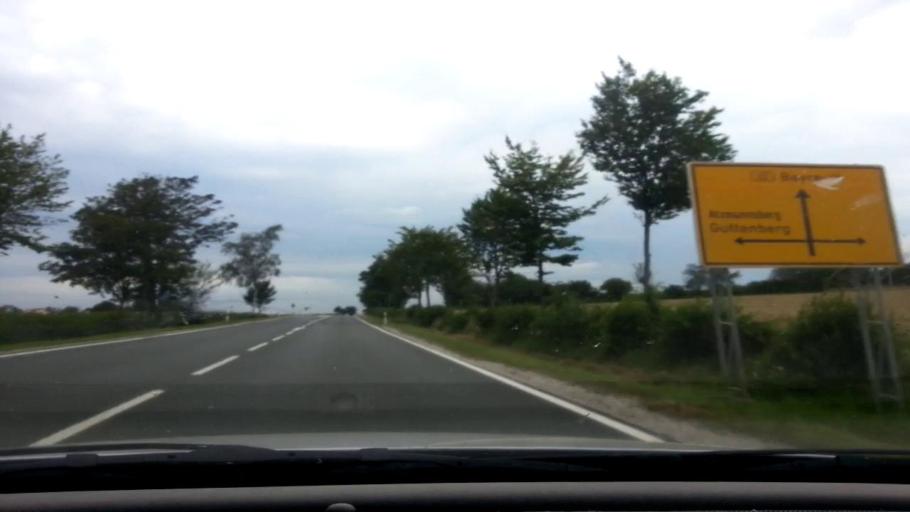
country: DE
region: Bavaria
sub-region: Upper Palatinate
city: Erbendorf
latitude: 49.8518
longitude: 11.9804
